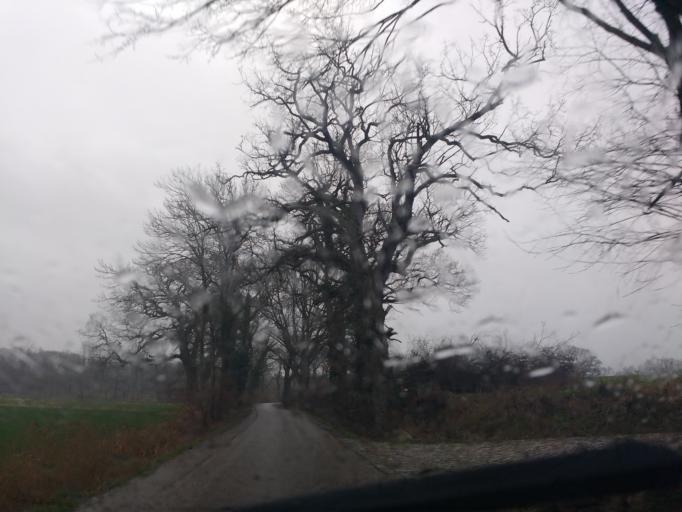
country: DE
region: Schleswig-Holstein
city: Wangels
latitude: 54.3041
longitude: 10.7553
